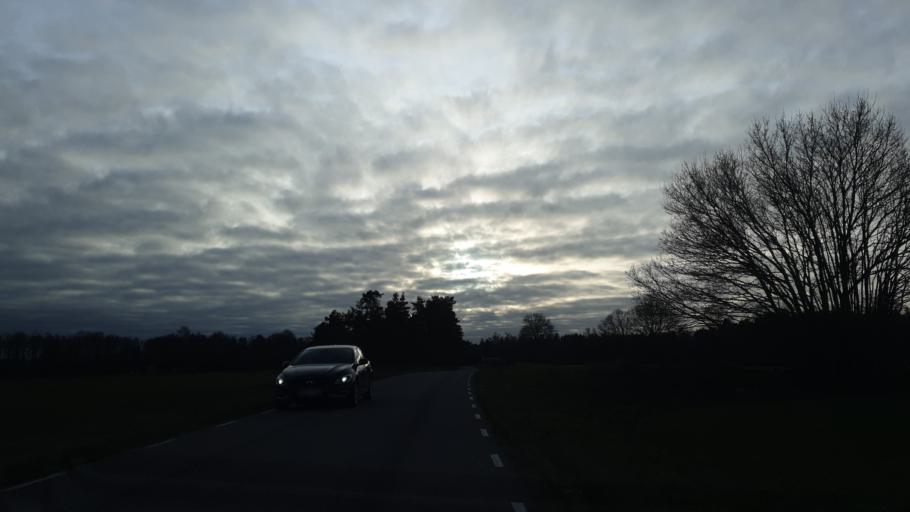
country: SE
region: Kalmar
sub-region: Torsas Kommun
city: Torsas
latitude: 56.3145
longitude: 16.0359
